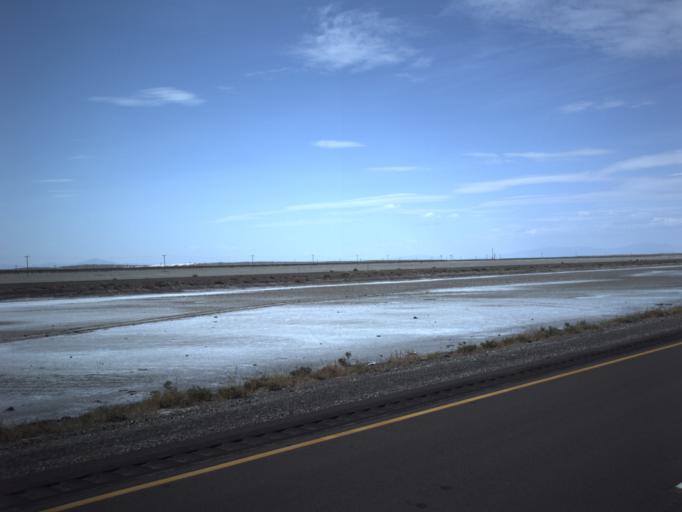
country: US
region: Utah
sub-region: Tooele County
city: Wendover
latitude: 40.7278
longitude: -113.2892
